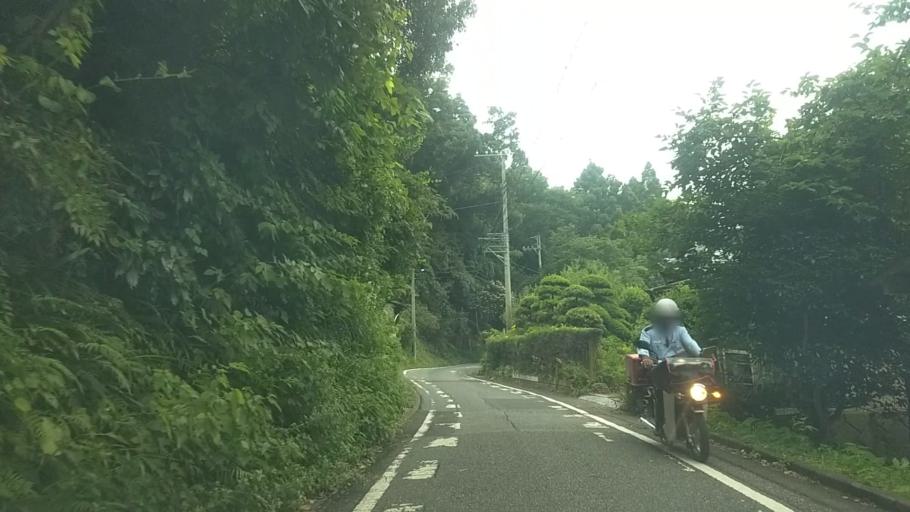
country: JP
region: Chiba
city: Kawaguchi
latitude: 35.2547
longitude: 140.0622
